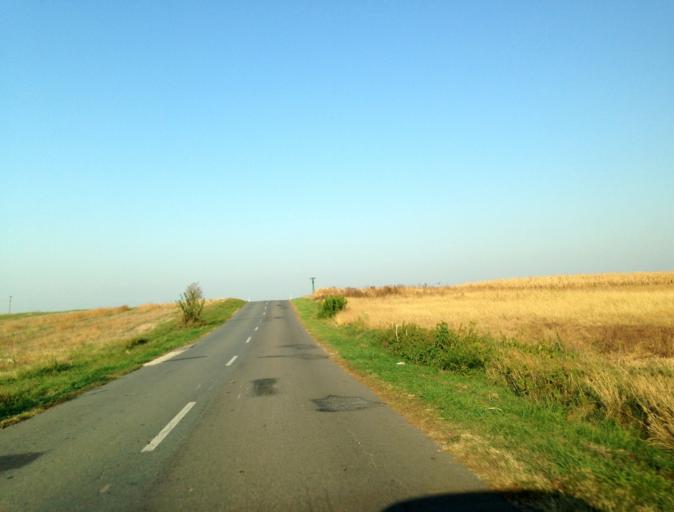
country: SK
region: Nitriansky
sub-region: Okres Komarno
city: Hurbanovo
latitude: 47.9052
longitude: 18.2823
